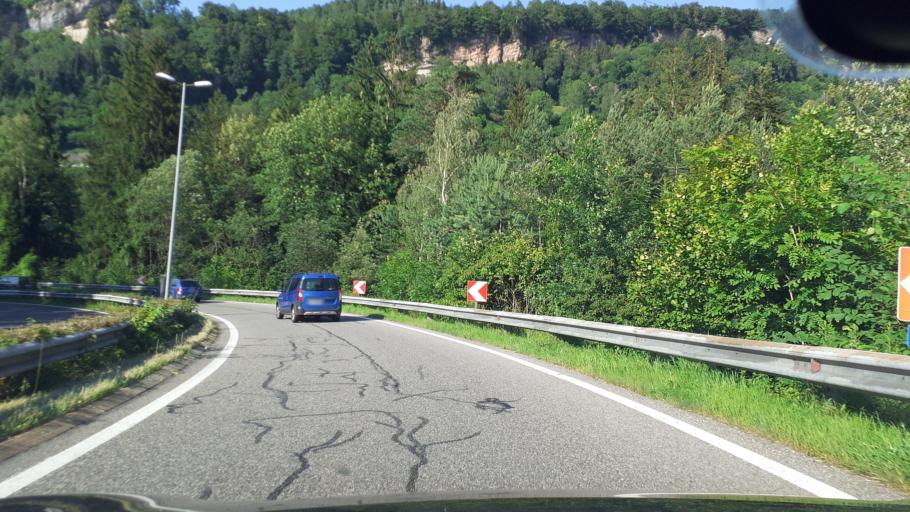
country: AT
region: Vorarlberg
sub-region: Politischer Bezirk Bregenz
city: Lauterach
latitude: 47.4849
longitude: 9.7449
